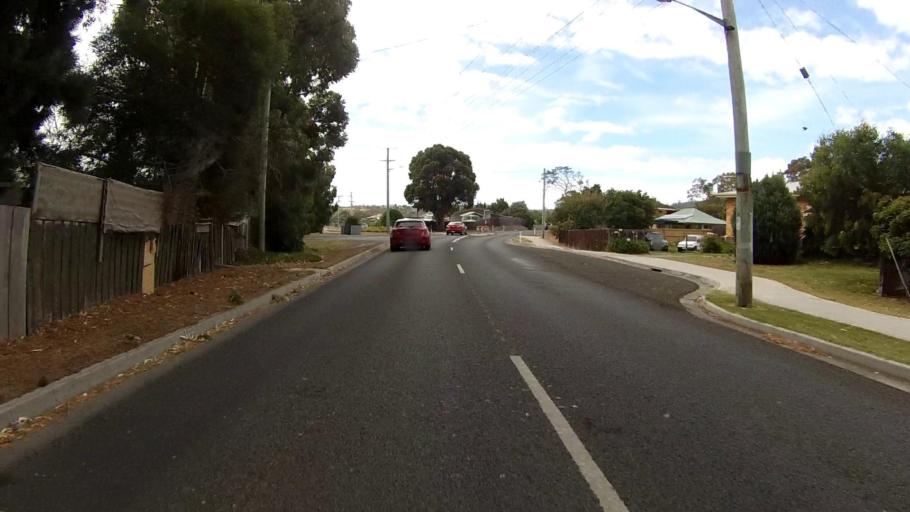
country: AU
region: Tasmania
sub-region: Sorell
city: Sorell
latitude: -42.8544
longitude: 147.6194
